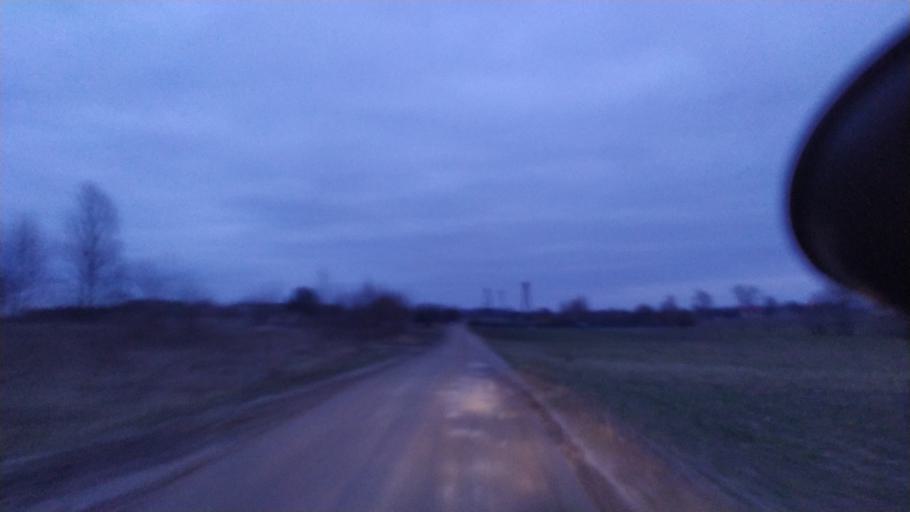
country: PL
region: Lublin Voivodeship
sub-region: Powiat lubartowski
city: Kamionka
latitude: 51.3947
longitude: 22.4173
